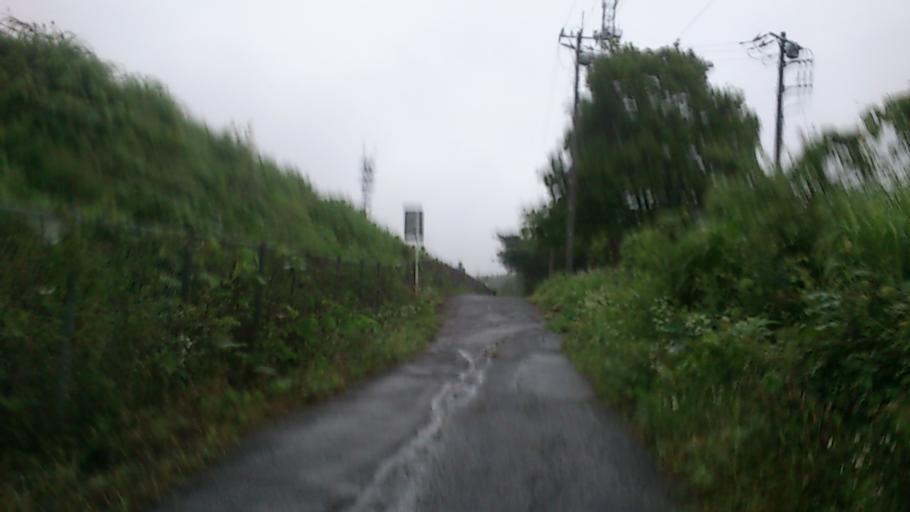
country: JP
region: Tochigi
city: Otawara
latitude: 36.9264
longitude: 139.9597
